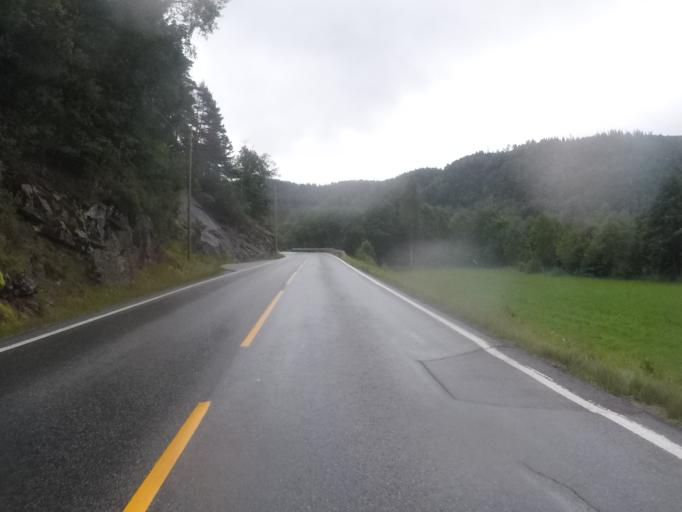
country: NO
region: Vest-Agder
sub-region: Songdalen
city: Nodeland
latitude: 58.1786
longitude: 7.8157
